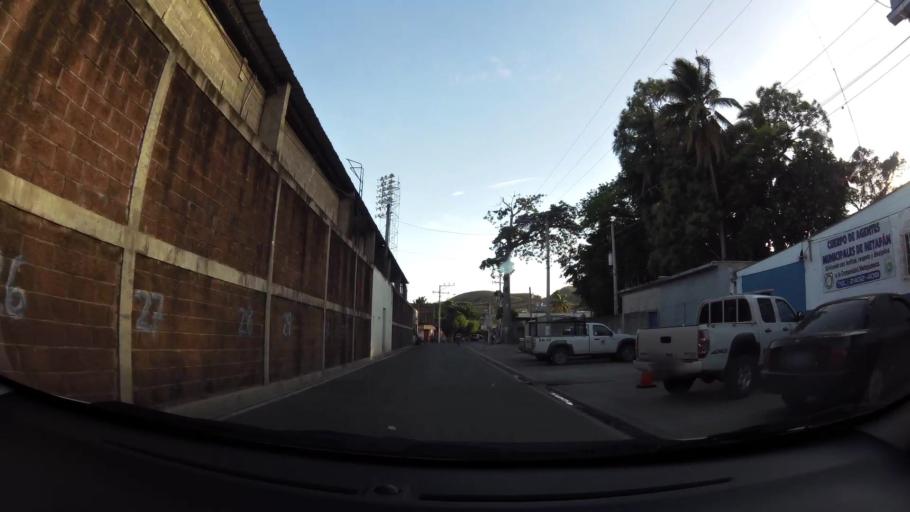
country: SV
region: Santa Ana
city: Metapan
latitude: 14.3321
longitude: -89.4495
